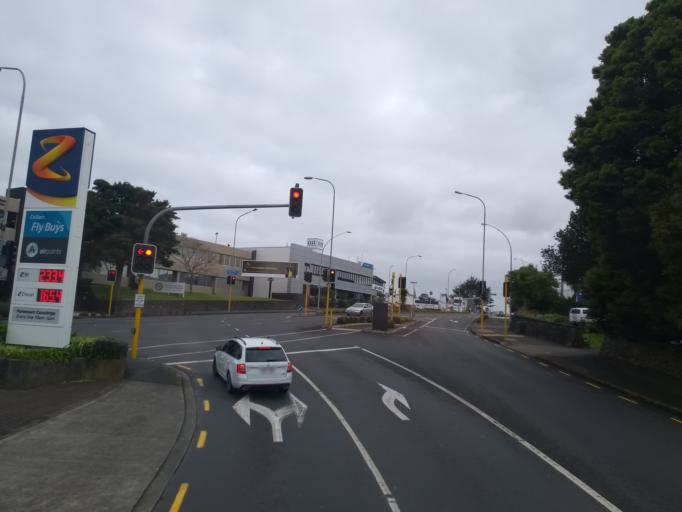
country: NZ
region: Auckland
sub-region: Auckland
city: Auckland
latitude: -36.8947
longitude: 174.8001
